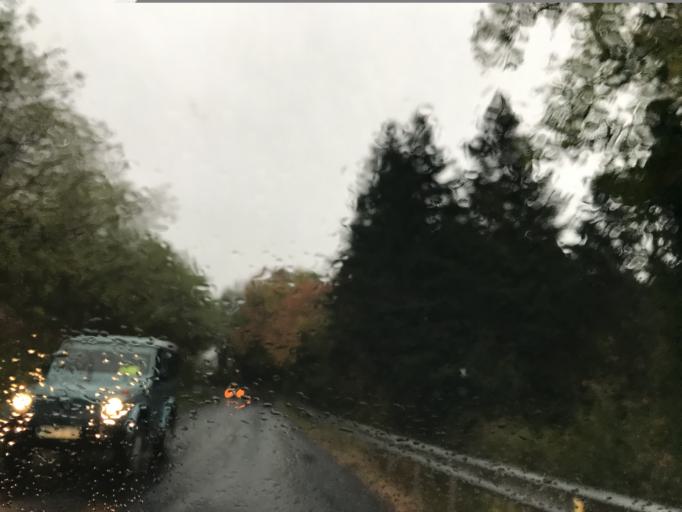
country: FR
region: Auvergne
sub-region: Departement du Puy-de-Dome
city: Courpiere
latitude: 45.7529
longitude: 3.5537
